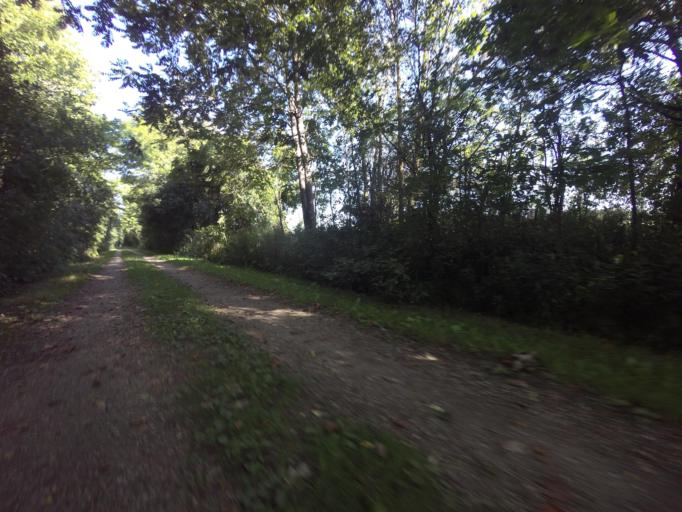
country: CA
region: Ontario
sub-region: Wellington County
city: Guelph
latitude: 43.6549
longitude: -80.4215
